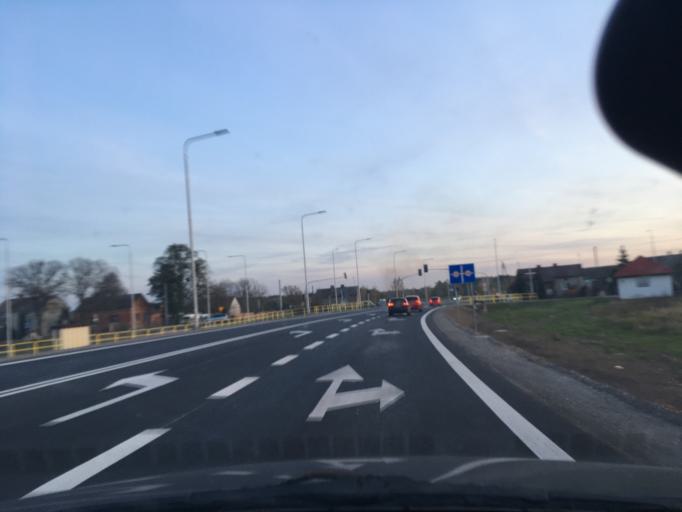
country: PL
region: Masovian Voivodeship
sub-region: Powiat plocki
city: Wyszogrod
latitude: 52.3576
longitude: 20.2080
